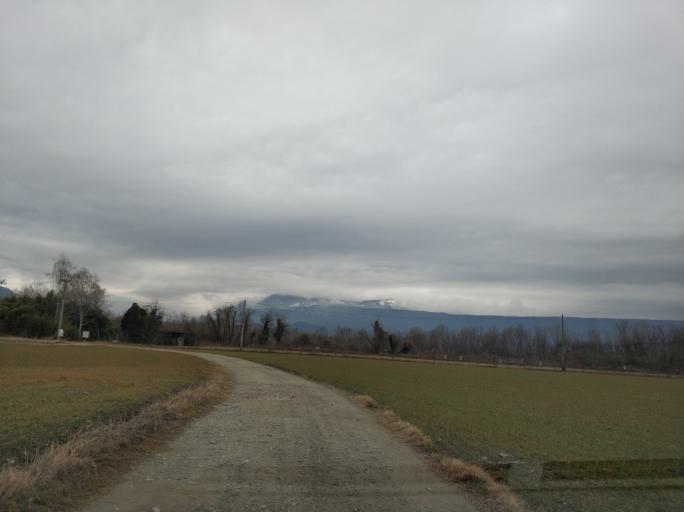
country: IT
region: Piedmont
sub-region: Provincia di Torino
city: Ivrea
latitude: 45.4545
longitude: 7.8887
